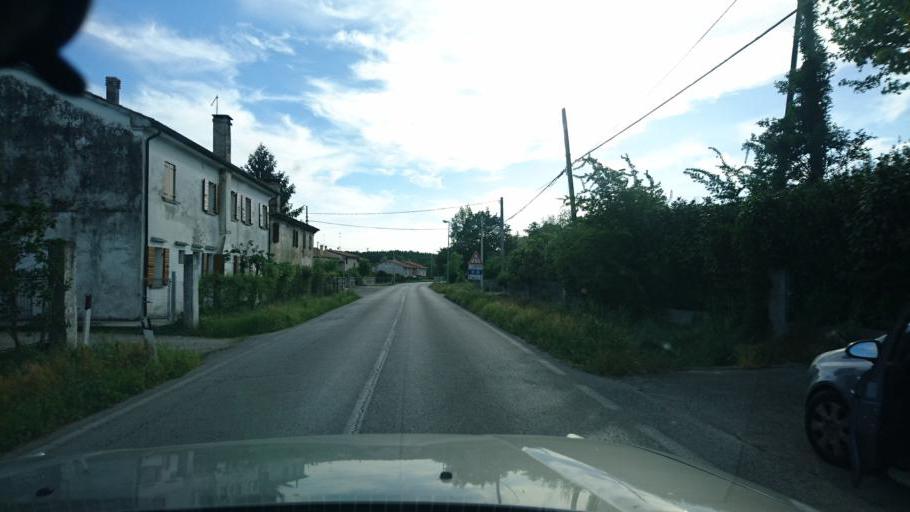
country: IT
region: Veneto
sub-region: Provincia di Treviso
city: Santa Cristina
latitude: 45.6425
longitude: 12.1167
